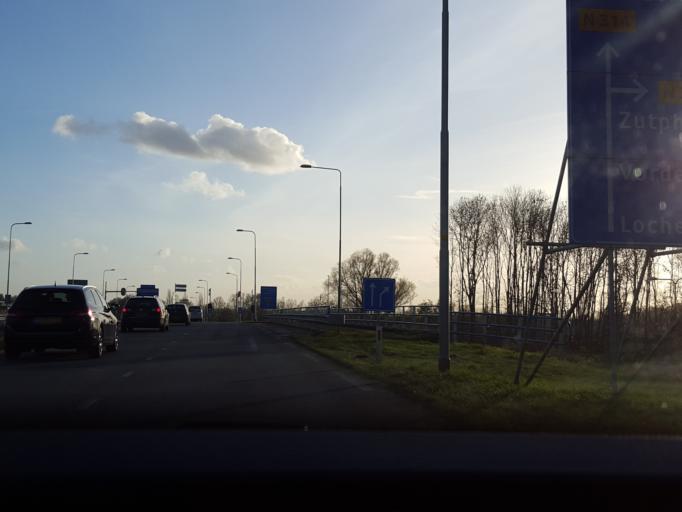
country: NL
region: Gelderland
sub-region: Gemeente Zutphen
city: Leesten
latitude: 52.1224
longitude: 6.2158
